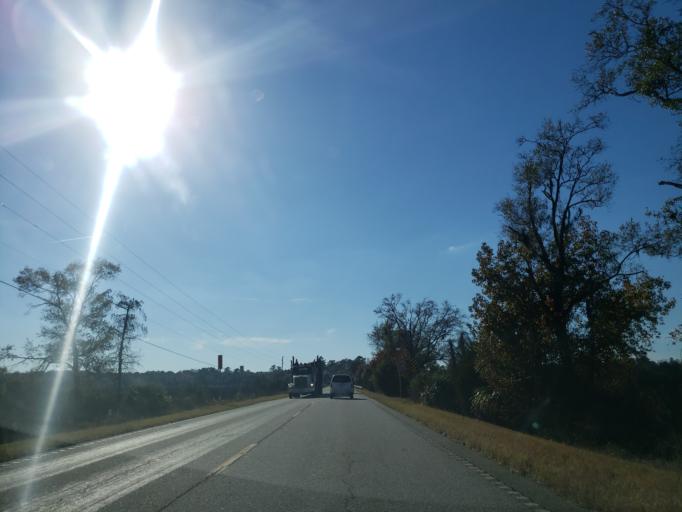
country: US
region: Georgia
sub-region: Glynn County
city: Dock Junction
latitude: 31.2669
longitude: -81.5901
